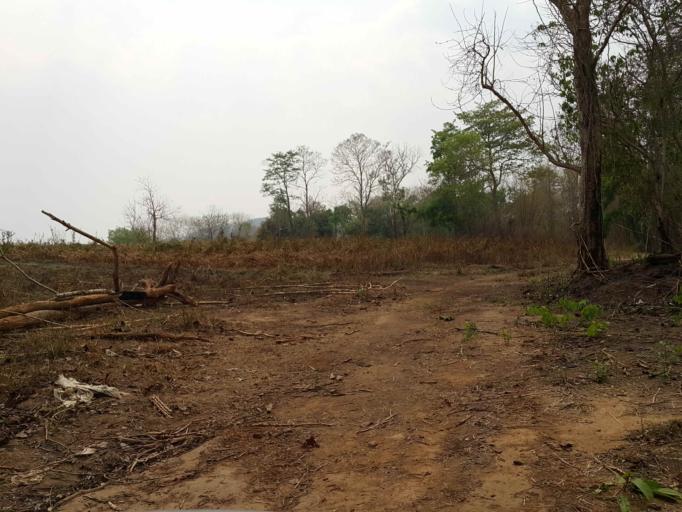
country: TH
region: Chiang Mai
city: Mae Taeng
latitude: 19.1174
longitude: 98.9902
